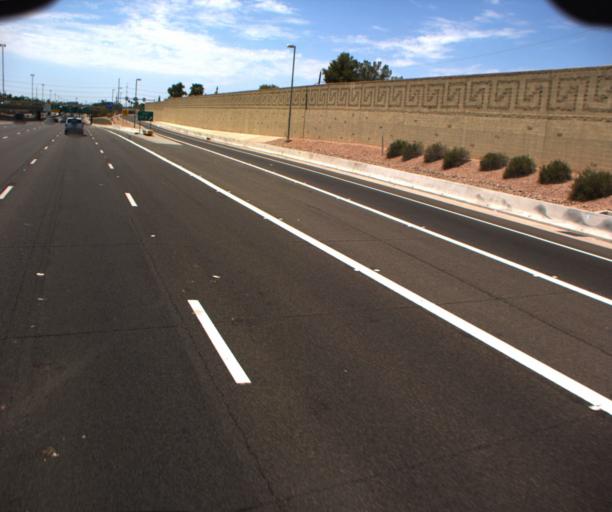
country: US
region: Arizona
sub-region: Maricopa County
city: Tempe Junction
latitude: 33.3858
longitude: -111.9358
